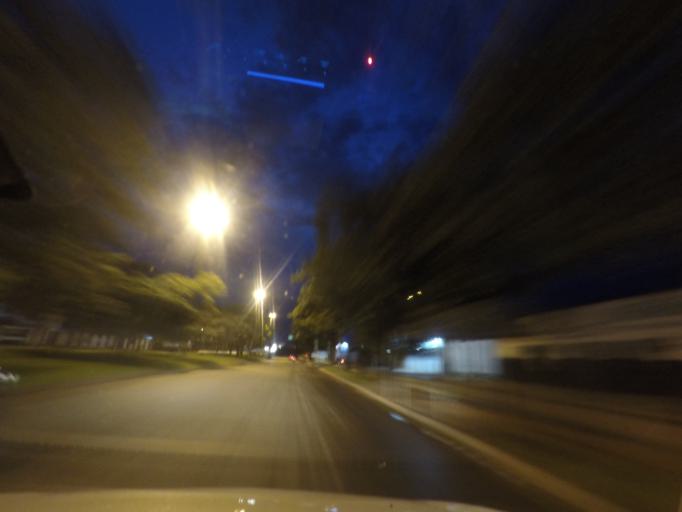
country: BR
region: Goias
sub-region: Goiania
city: Goiania
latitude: -16.6983
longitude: -49.3304
